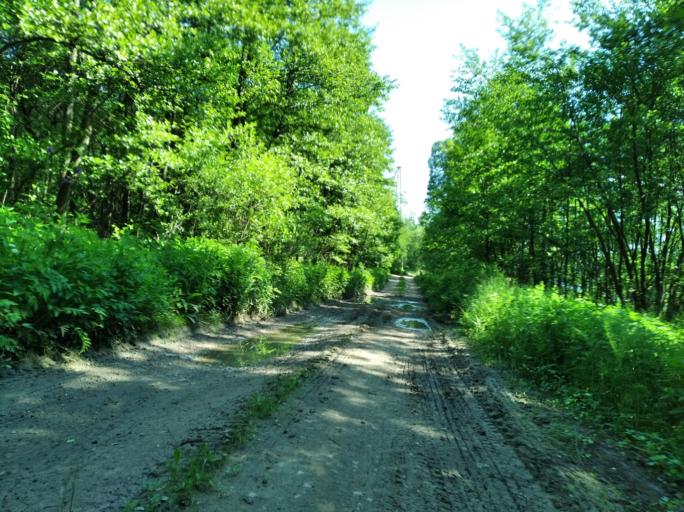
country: PL
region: Subcarpathian Voivodeship
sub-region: Powiat krosnienski
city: Odrzykon
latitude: 49.7707
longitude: 21.7605
